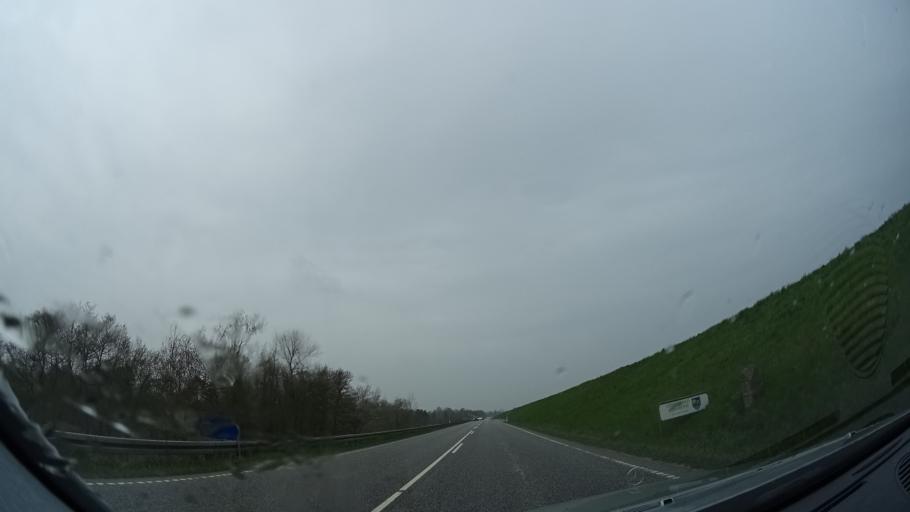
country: DK
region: Zealand
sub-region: Holbaek Kommune
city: Holbaek
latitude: 55.7745
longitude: 11.6233
